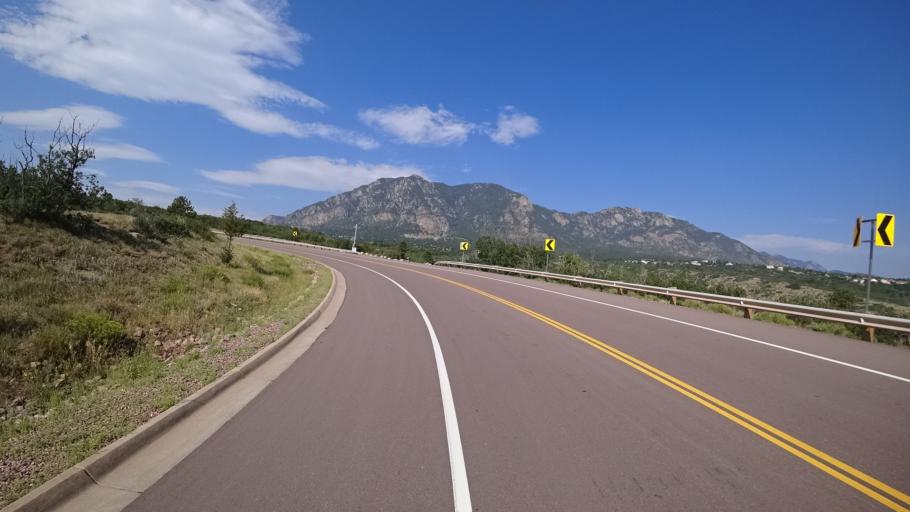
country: US
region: Colorado
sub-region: El Paso County
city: Fort Carson
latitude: 38.7505
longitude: -104.8195
